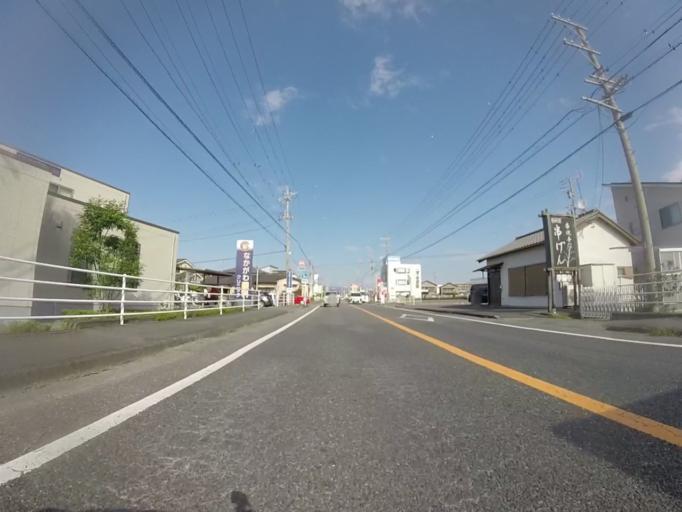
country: JP
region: Shizuoka
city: Fujieda
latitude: 34.8372
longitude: 138.2652
